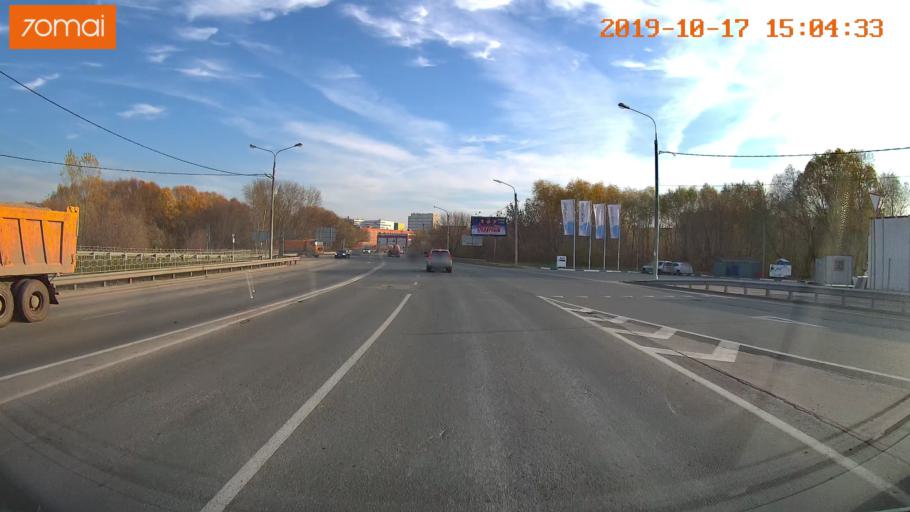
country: RU
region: Rjazan
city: Ryazan'
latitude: 54.6390
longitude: 39.7202
